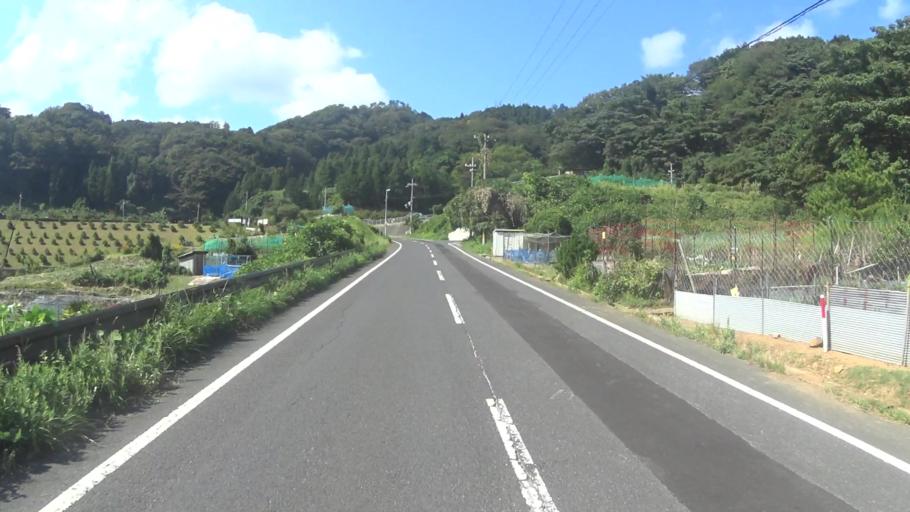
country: JP
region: Kyoto
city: Miyazu
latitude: 35.6753
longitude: 135.2953
